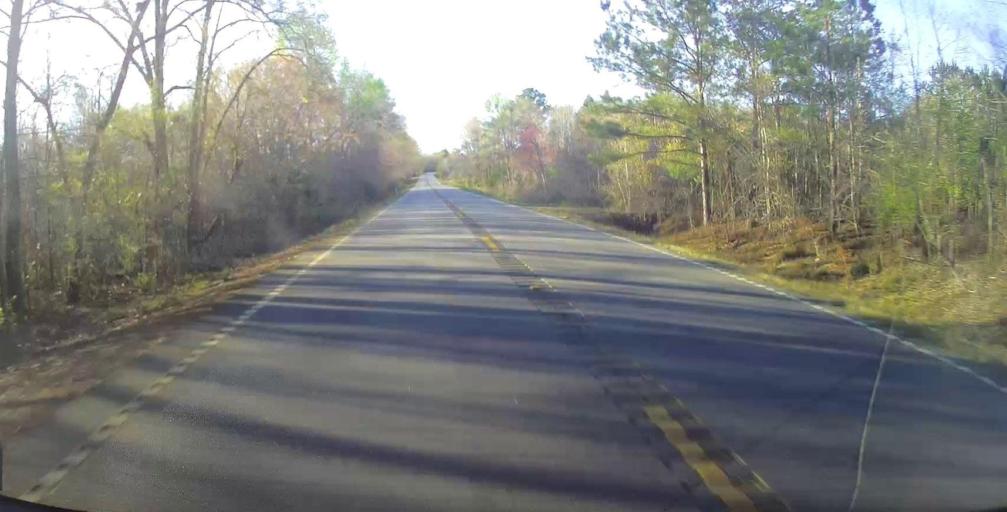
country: US
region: Georgia
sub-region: Wilcox County
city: Abbeville
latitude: 32.1188
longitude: -83.3260
